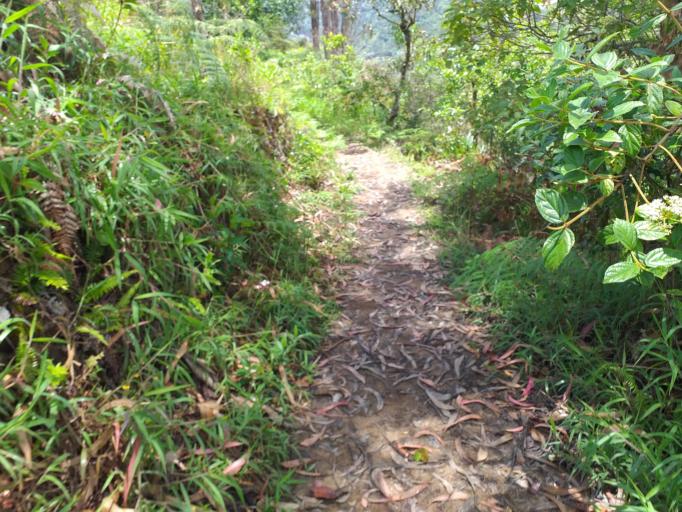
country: CO
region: Cundinamarca
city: Tenza
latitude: 5.1111
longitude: -73.4478
